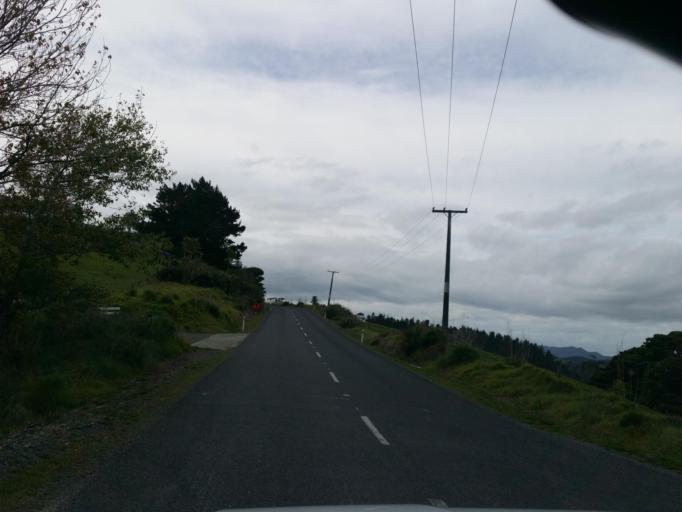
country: NZ
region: Northland
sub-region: Kaipara District
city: Dargaville
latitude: -35.9552
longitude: 173.9223
